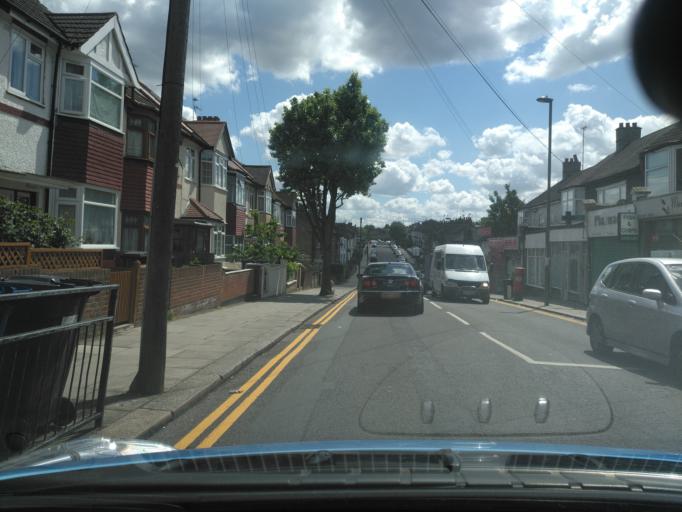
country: GB
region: England
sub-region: Greater London
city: Hendon
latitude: 51.6001
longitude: -0.1818
